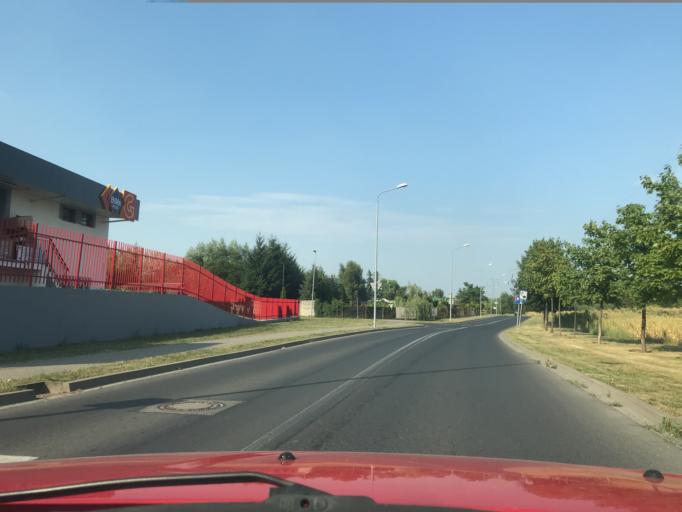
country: PL
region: Greater Poland Voivodeship
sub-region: Powiat poznanski
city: Plewiska
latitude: 52.3627
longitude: 16.8513
